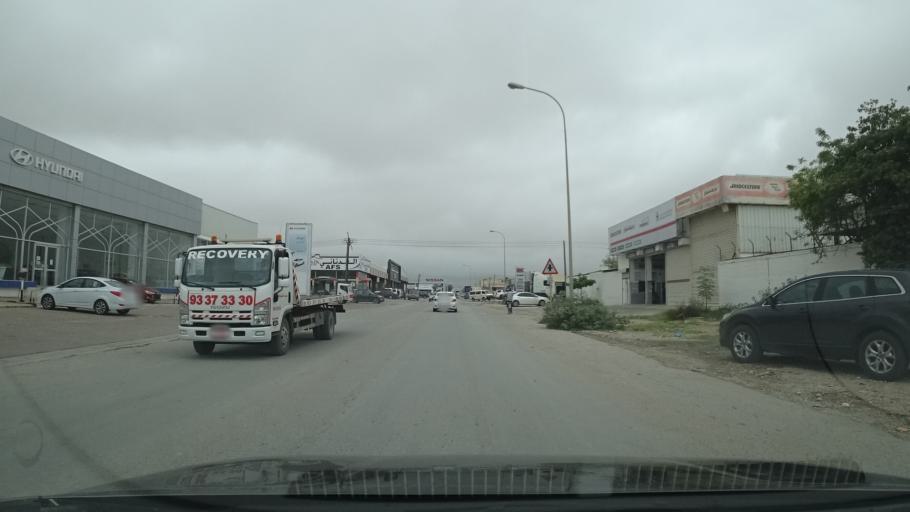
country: OM
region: Zufar
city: Salalah
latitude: 17.0163
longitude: 54.0451
